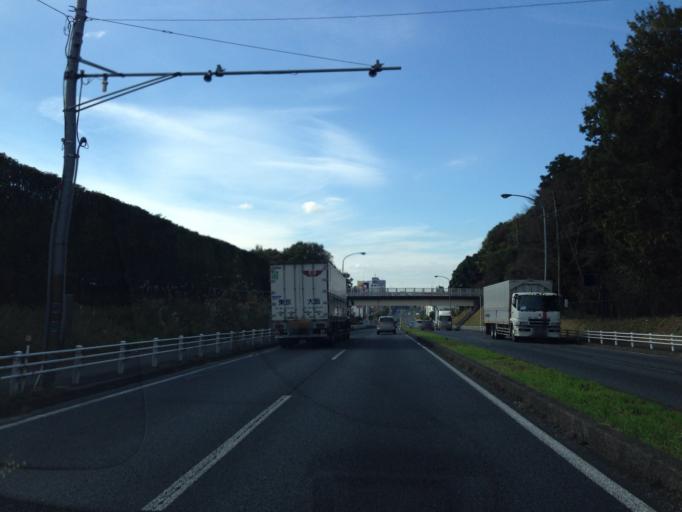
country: JP
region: Chiba
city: Abiko
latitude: 35.8771
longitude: 140.0247
